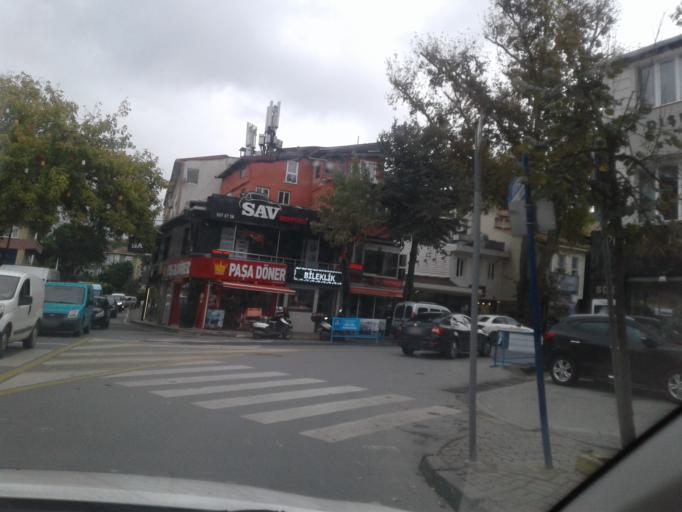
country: TR
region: Istanbul
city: UEskuedar
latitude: 41.0498
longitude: 29.0542
